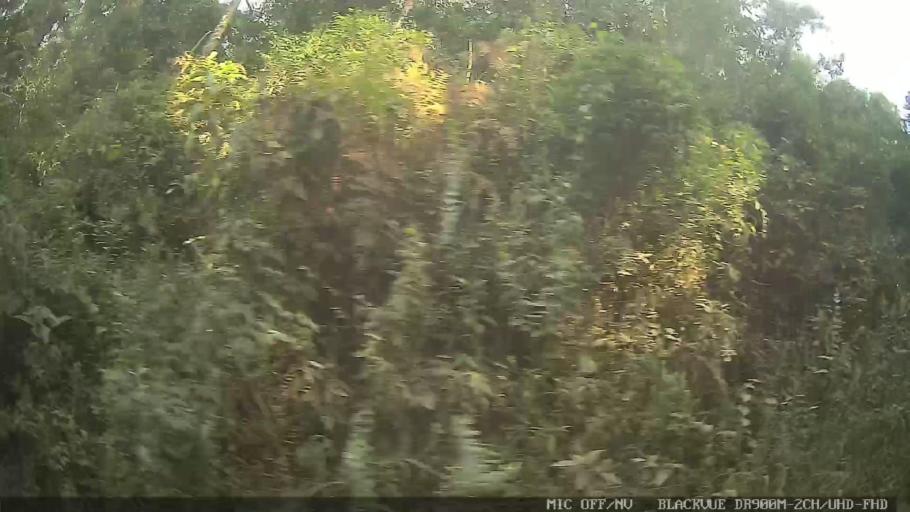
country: BR
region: Sao Paulo
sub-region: Atibaia
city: Atibaia
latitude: -23.1578
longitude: -46.5147
